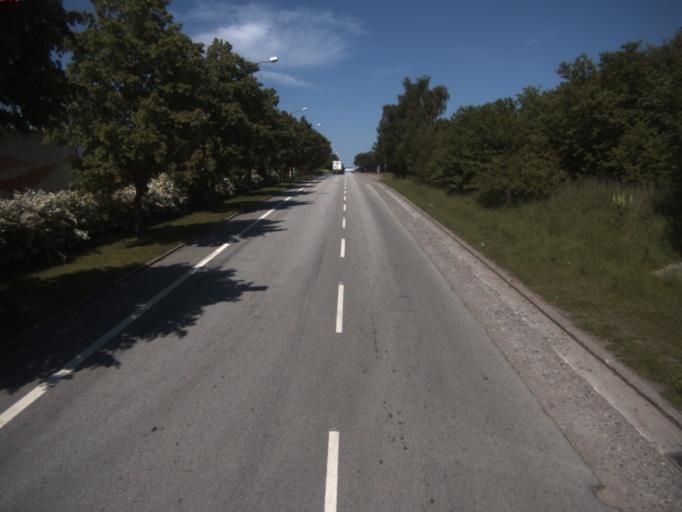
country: SE
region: Skane
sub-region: Helsingborg
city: Gantofta
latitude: 56.0054
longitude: 12.7765
